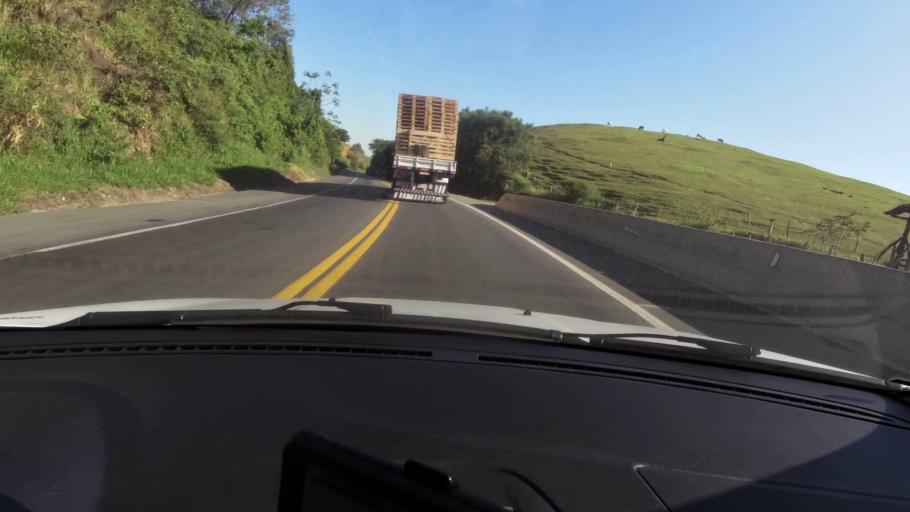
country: BR
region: Espirito Santo
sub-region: Alfredo Chaves
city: Alfredo Chaves
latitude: -20.6675
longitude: -40.6628
